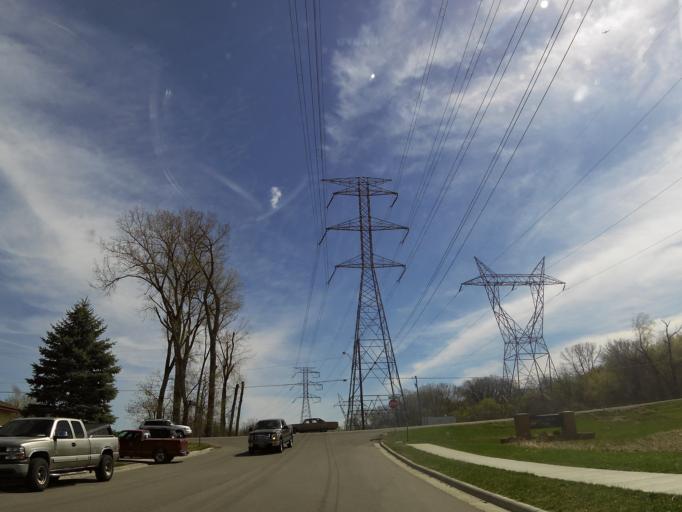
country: US
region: Minnesota
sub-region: Scott County
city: Savage
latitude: 44.7715
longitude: -93.3368
